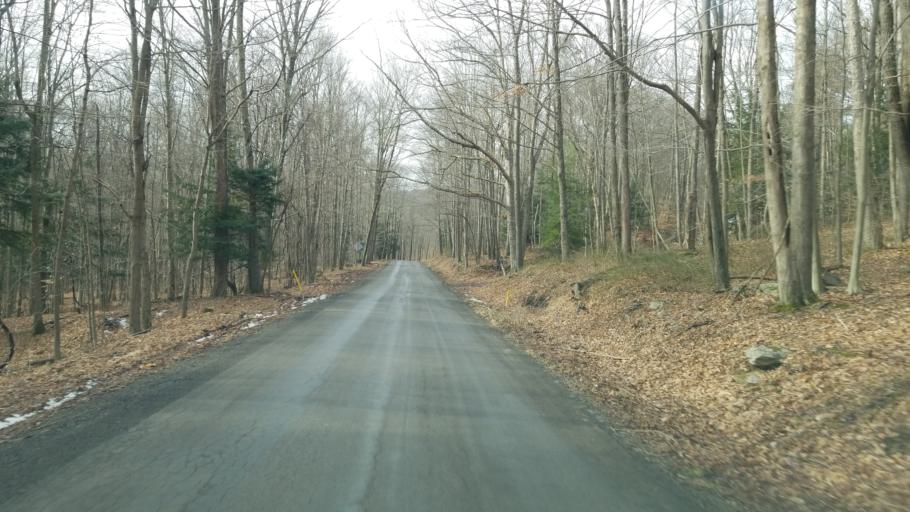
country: US
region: Pennsylvania
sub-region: Indiana County
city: Johnsonburg
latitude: 40.8329
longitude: -78.9055
